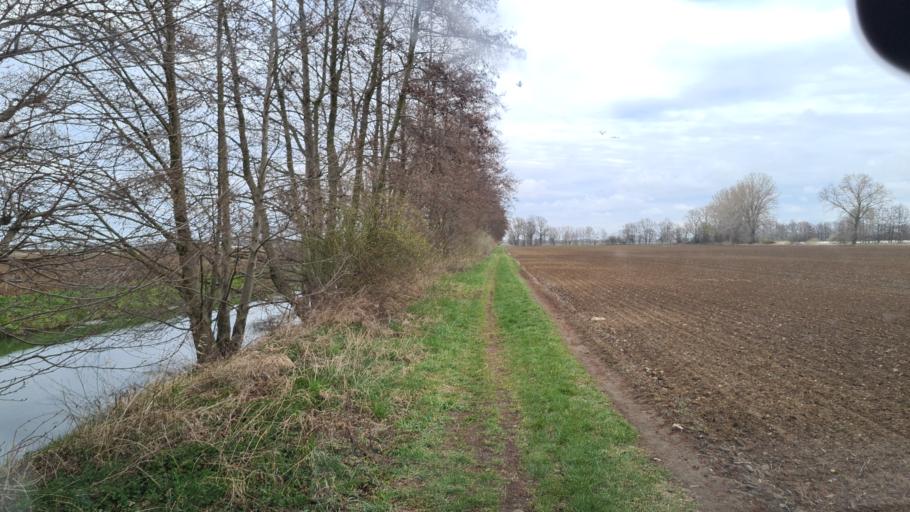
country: DE
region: Brandenburg
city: Doberlug-Kirchhain
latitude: 51.6510
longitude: 13.5607
